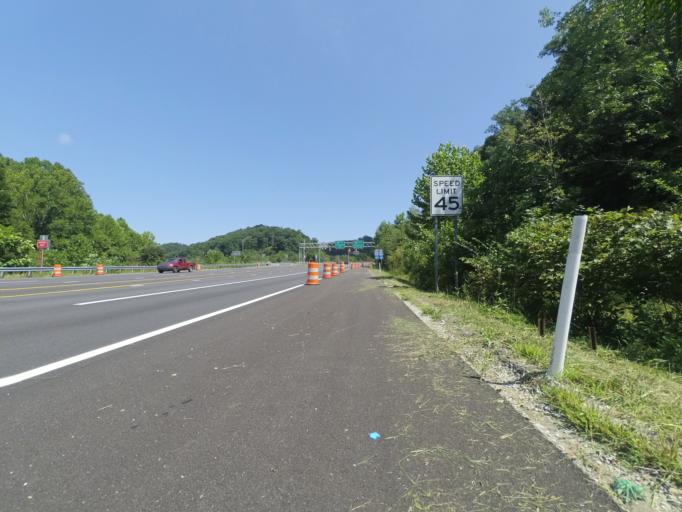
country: US
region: West Virginia
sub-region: Cabell County
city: Huntington
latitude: 38.3912
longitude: -82.4539
